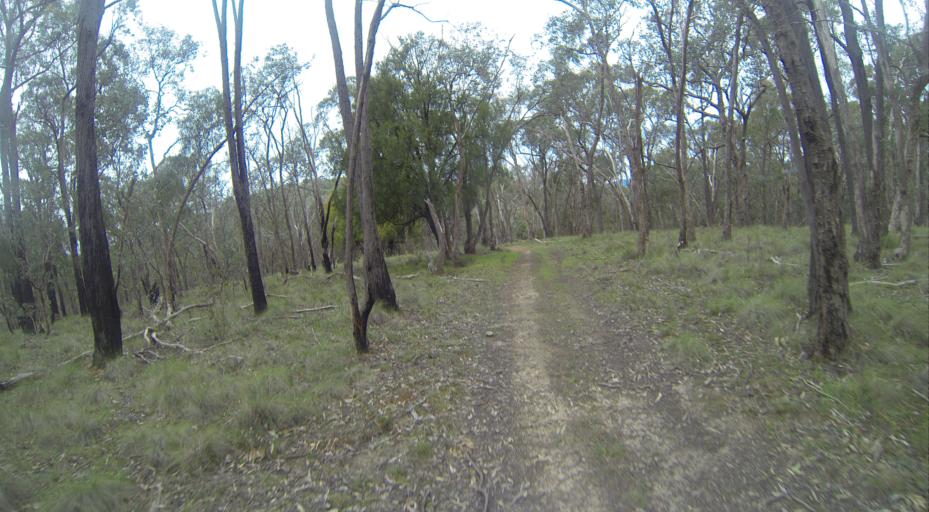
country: AU
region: Victoria
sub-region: Nillumbik
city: Saint Andrews
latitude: -37.6420
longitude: 145.3041
